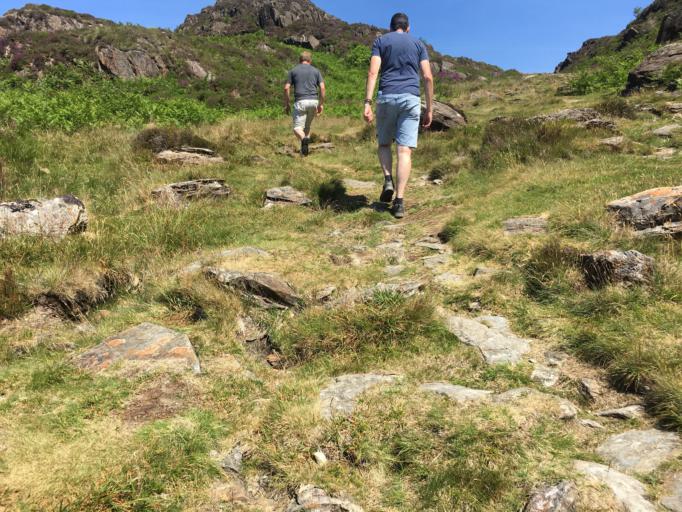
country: GB
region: Wales
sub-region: Gwynedd
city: Penrhyndeudraeth
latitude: 53.0094
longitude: -4.0805
